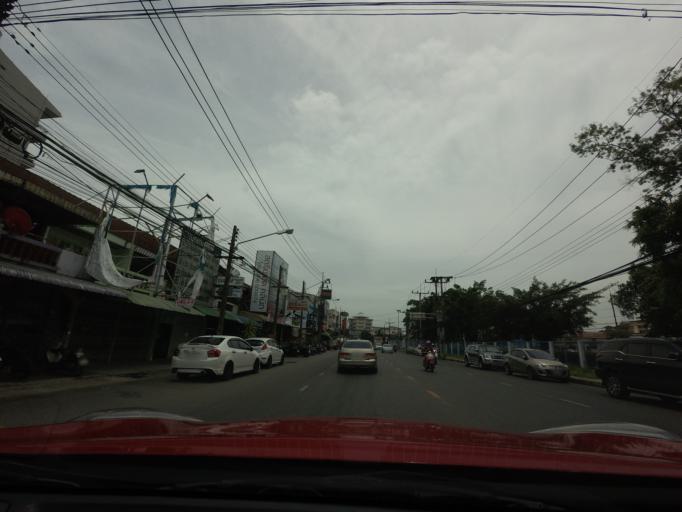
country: TH
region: Songkhla
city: Hat Yai
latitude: 7.0016
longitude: 100.4923
